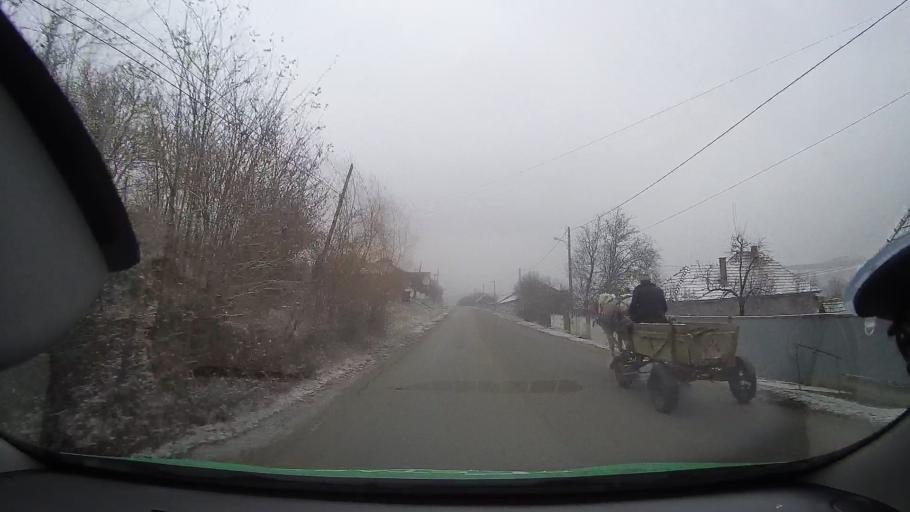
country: RO
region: Alba
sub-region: Comuna Noslac
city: Noslac
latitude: 46.3456
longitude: 23.9411
